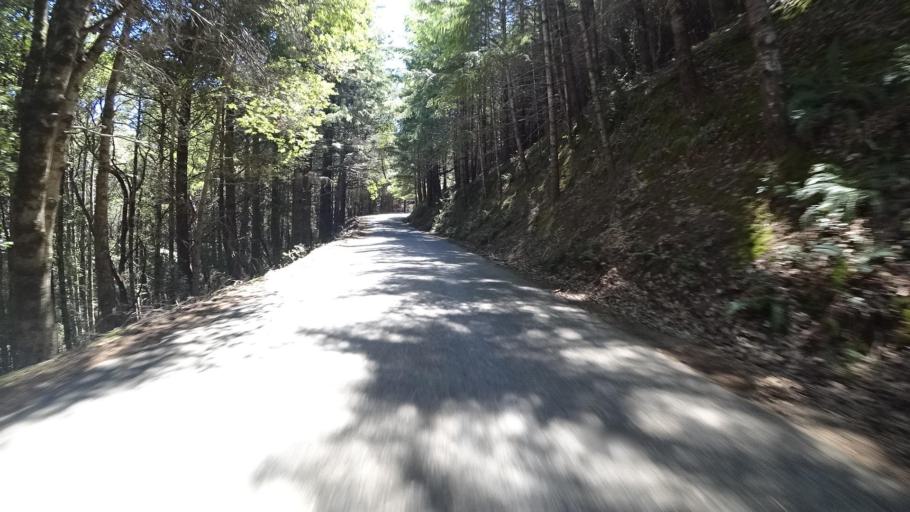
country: US
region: California
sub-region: Humboldt County
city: Redway
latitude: 40.1300
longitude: -123.9778
